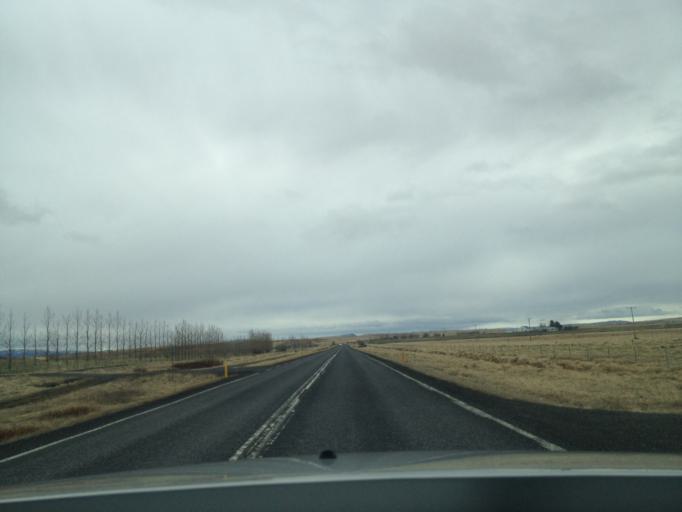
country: IS
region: South
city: Vestmannaeyjar
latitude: 63.8559
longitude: -20.4302
